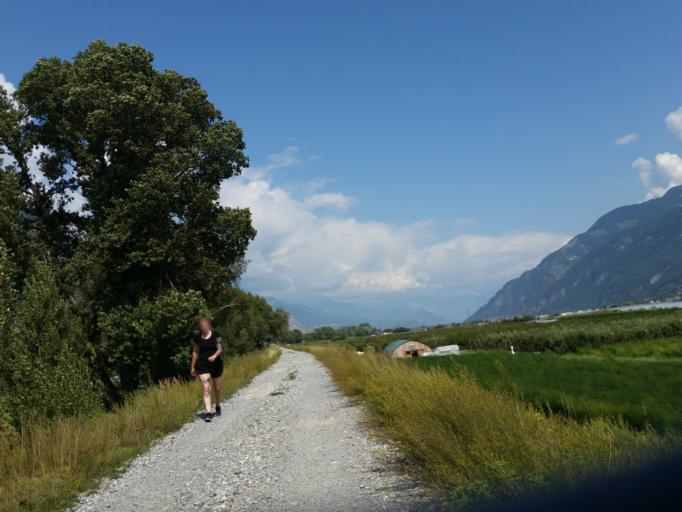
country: CH
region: Valais
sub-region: Martigny District
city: Charrat-les-Chenes
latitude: 46.1385
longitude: 7.1331
